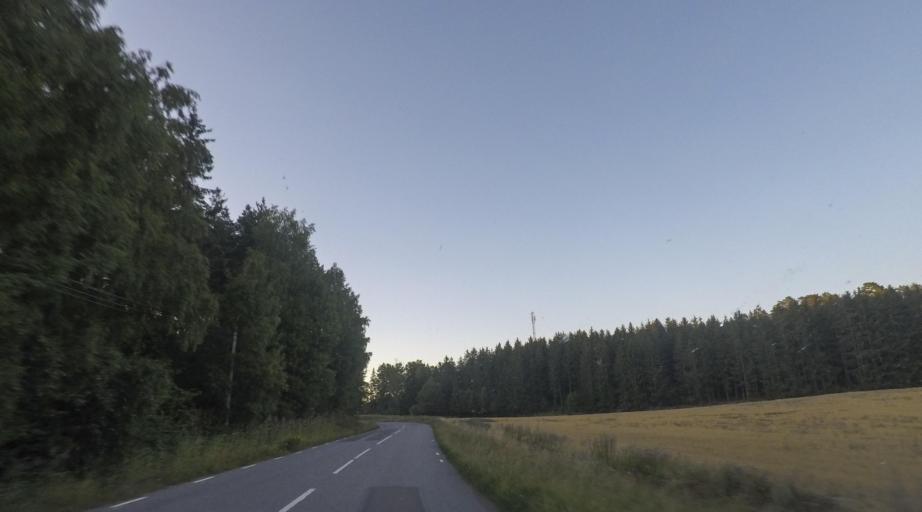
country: SE
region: Soedermanland
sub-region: Trosa Kommun
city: Trosa
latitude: 58.9711
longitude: 17.6938
